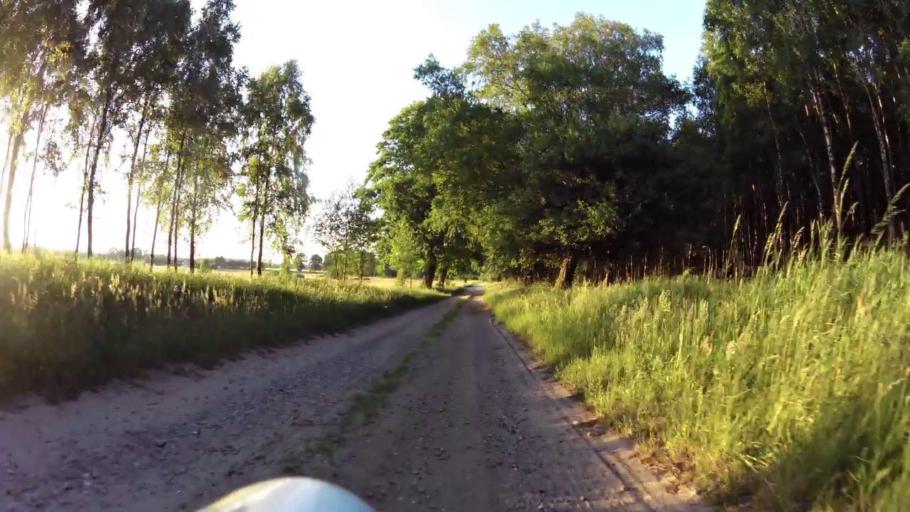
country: PL
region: West Pomeranian Voivodeship
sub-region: Powiat szczecinecki
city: Szczecinek
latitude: 53.8398
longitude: 16.6898
